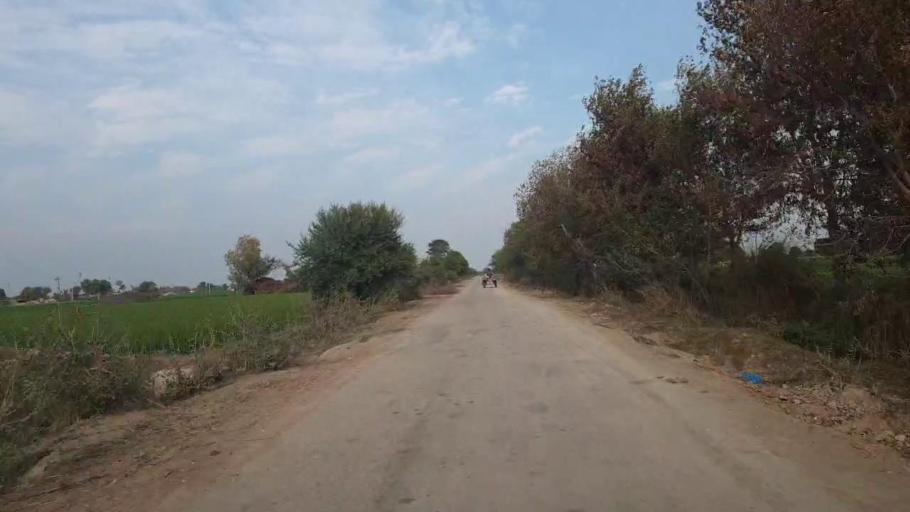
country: PK
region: Sindh
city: Shahdadpur
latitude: 26.0423
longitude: 68.5583
